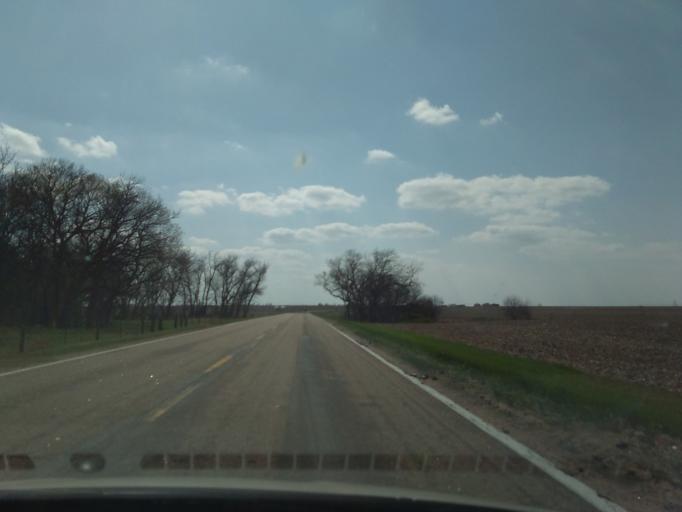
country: US
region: Nebraska
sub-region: Thayer County
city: Hebron
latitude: 40.1488
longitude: -97.6820
